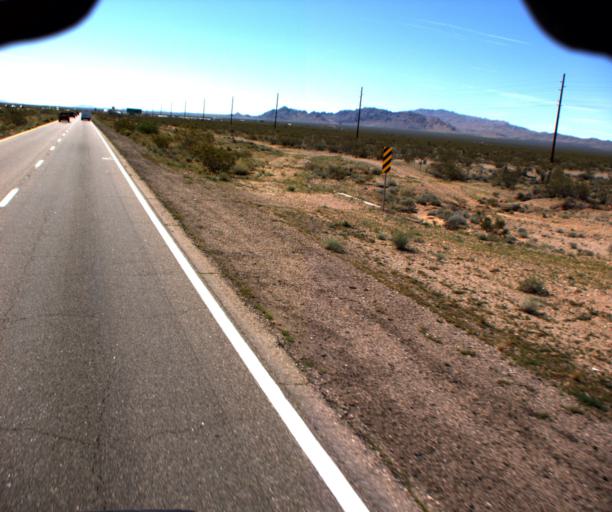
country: US
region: Arizona
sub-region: Mohave County
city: Dolan Springs
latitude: 35.7144
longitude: -114.4826
